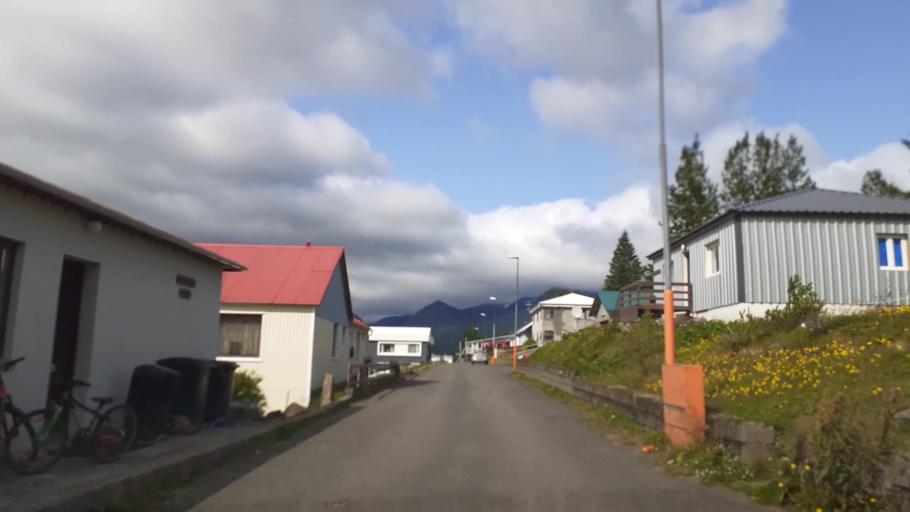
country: IS
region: East
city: Eskifjoerdur
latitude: 64.9270
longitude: -14.0008
